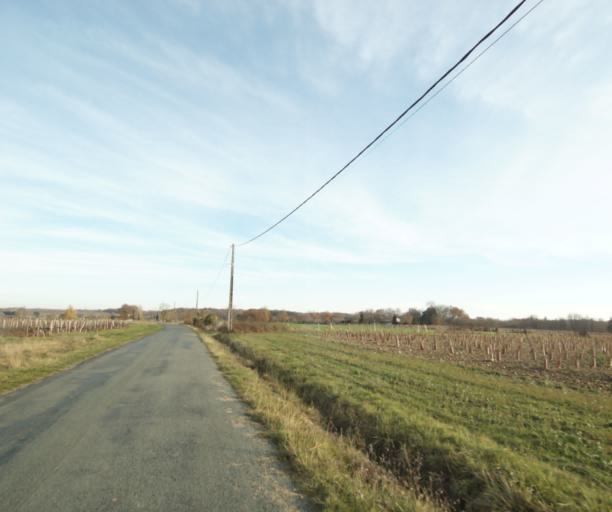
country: FR
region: Poitou-Charentes
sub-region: Departement de la Charente-Maritime
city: Chaniers
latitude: 45.7459
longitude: -0.5504
